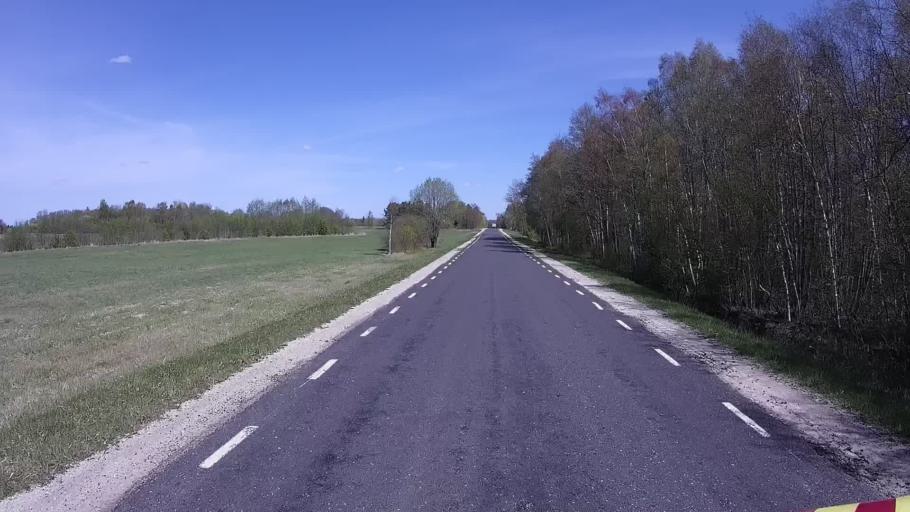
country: EE
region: Laeaene
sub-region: Ridala Parish
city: Uuemoisa
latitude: 59.0140
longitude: 23.7881
